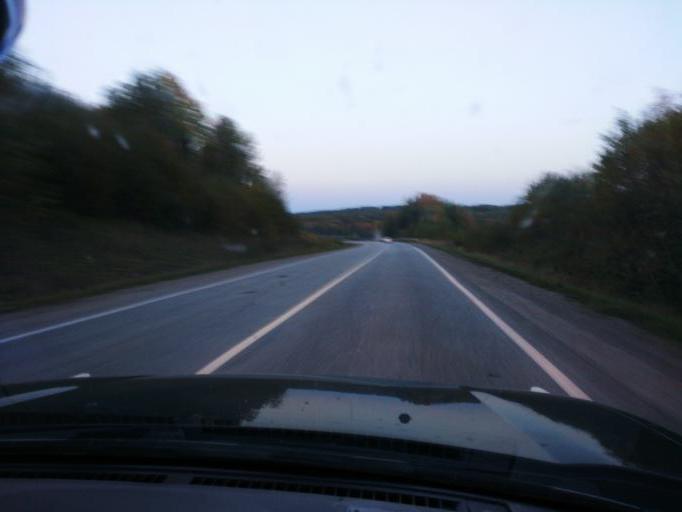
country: RU
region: Perm
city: Verkhnechusovskiye Gorodki
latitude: 58.2945
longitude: 56.8727
